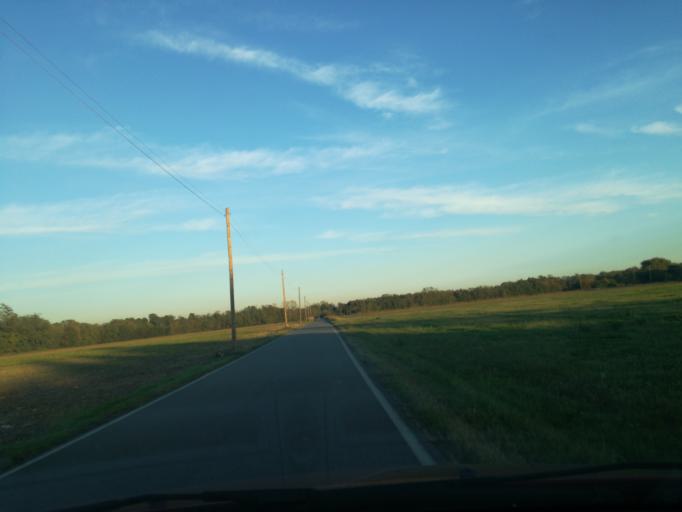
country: IT
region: Lombardy
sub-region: Provincia di Monza e Brianza
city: Burago di Molgora
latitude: 45.6049
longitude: 9.3963
